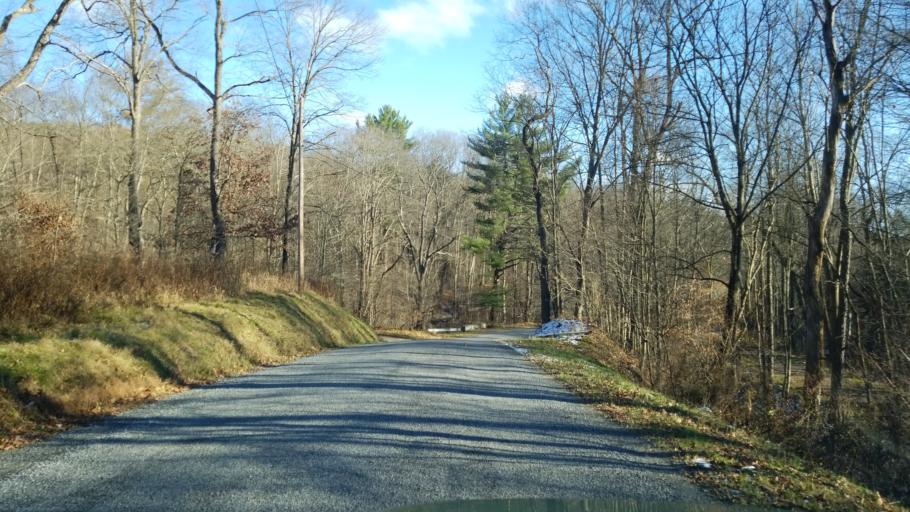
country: US
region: Pennsylvania
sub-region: Jefferson County
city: Brockway
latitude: 41.2785
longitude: -78.8180
